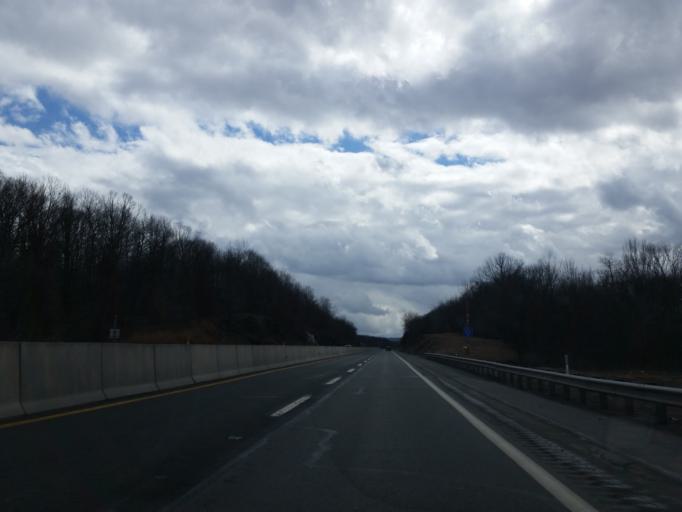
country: US
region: Pennsylvania
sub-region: Lackawanna County
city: Old Forge
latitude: 41.3696
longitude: -75.7199
